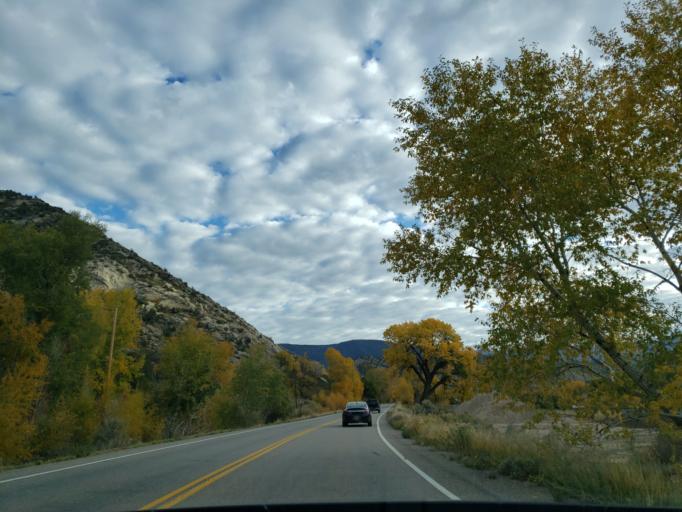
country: US
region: Colorado
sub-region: Garfield County
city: New Castle
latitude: 39.5654
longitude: -107.5519
